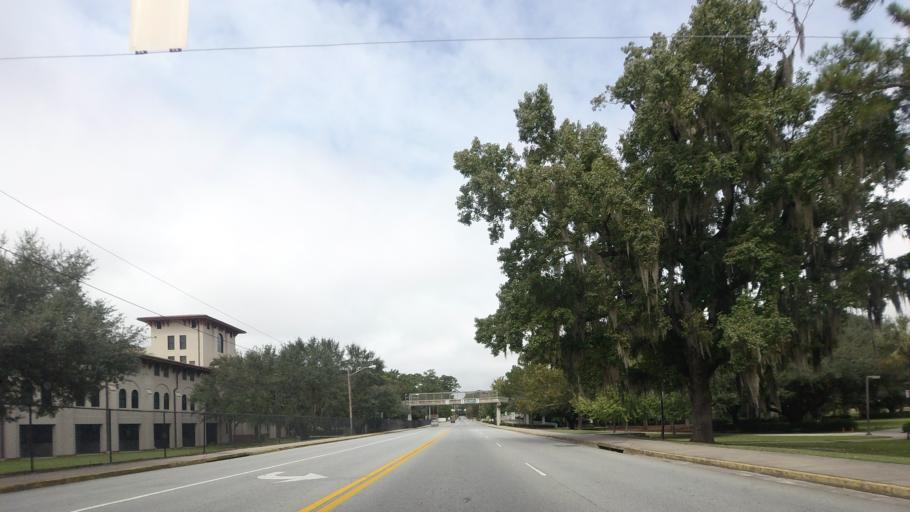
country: US
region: Georgia
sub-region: Lowndes County
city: Valdosta
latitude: 30.8451
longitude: -83.2896
